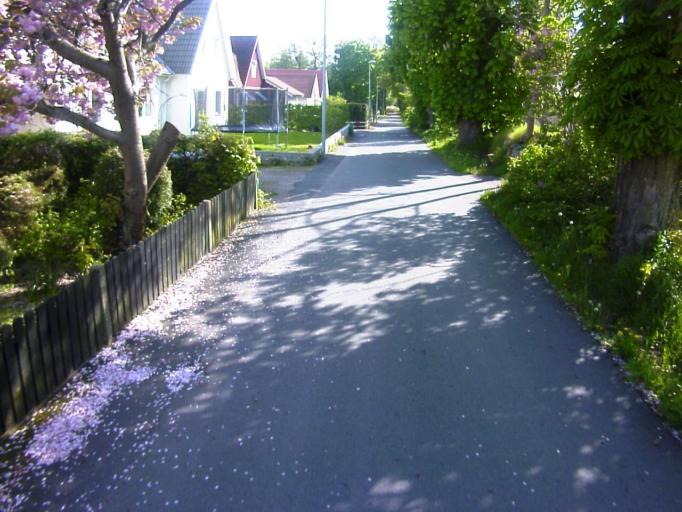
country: SE
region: Blekinge
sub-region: Solvesborgs Kommun
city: Soelvesborg
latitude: 56.0582
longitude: 14.5982
